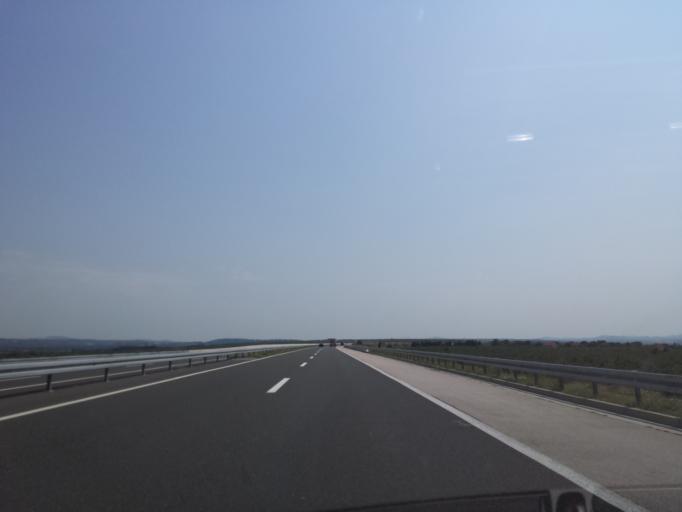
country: HR
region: Zadarska
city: Polaca
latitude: 44.0573
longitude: 15.5374
